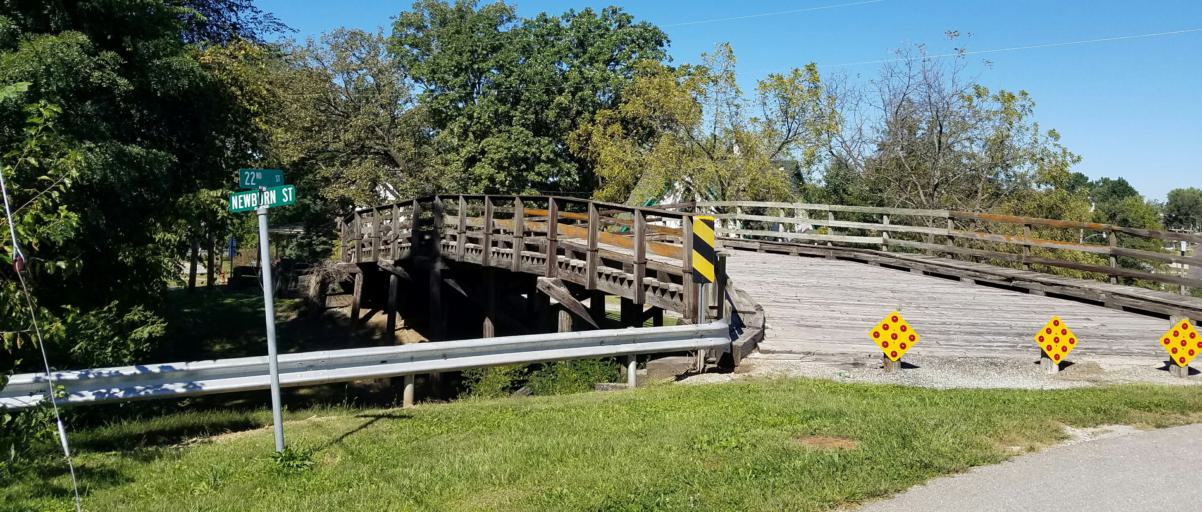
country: US
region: Missouri
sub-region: Harrison County
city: Bethany
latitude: 40.2663
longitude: -94.0298
